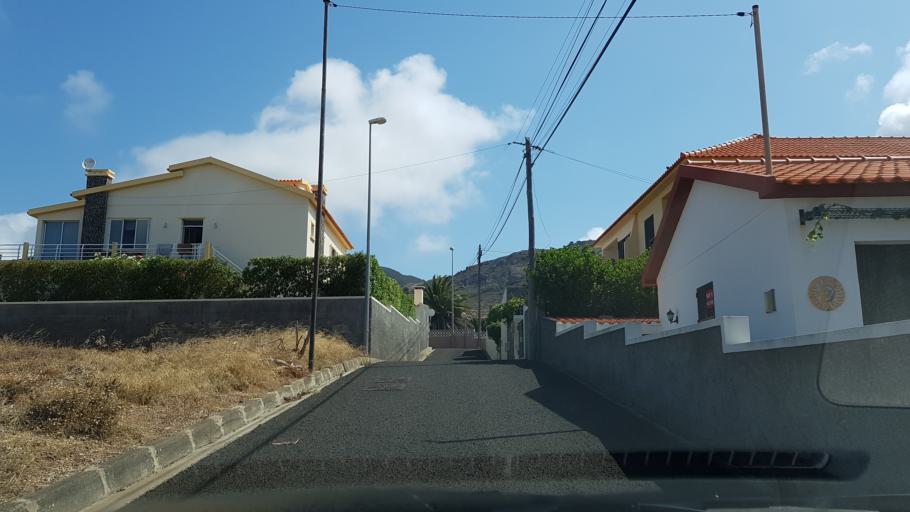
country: PT
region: Madeira
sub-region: Porto Santo
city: Vila de Porto Santo
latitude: 33.0654
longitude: -16.3289
